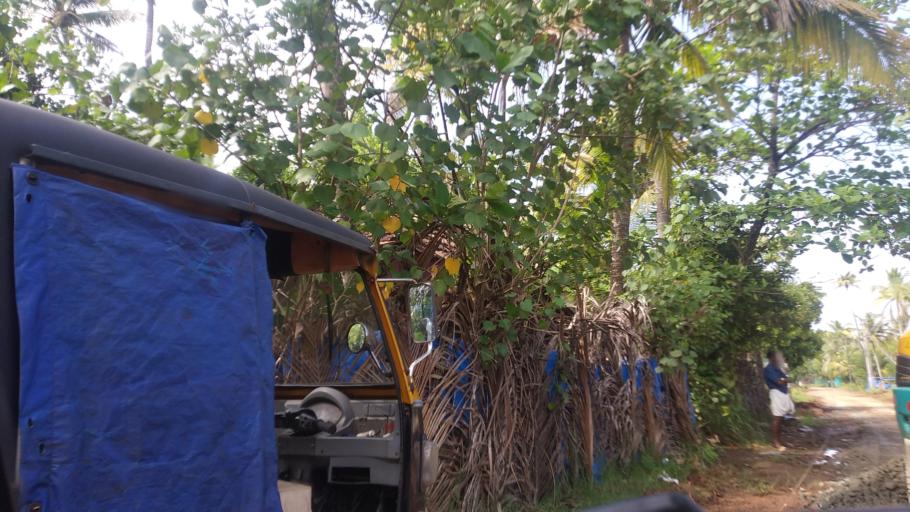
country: IN
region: Kerala
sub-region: Ernakulam
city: Elur
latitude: 10.0567
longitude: 76.2015
